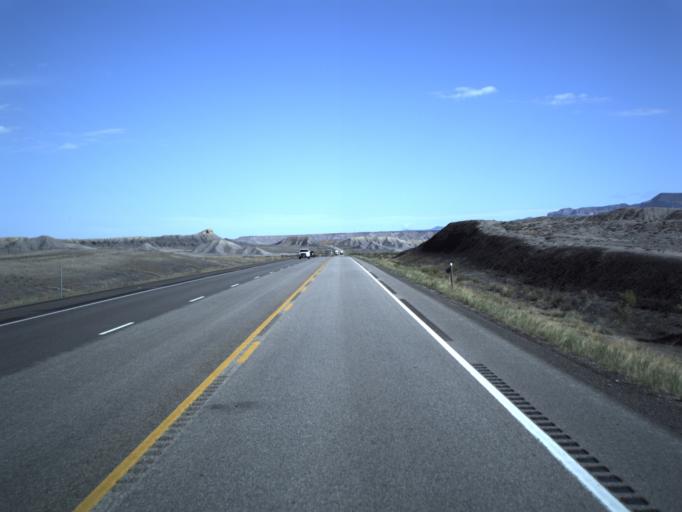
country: US
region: Utah
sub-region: Carbon County
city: East Carbon City
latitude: 39.3182
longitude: -110.3638
